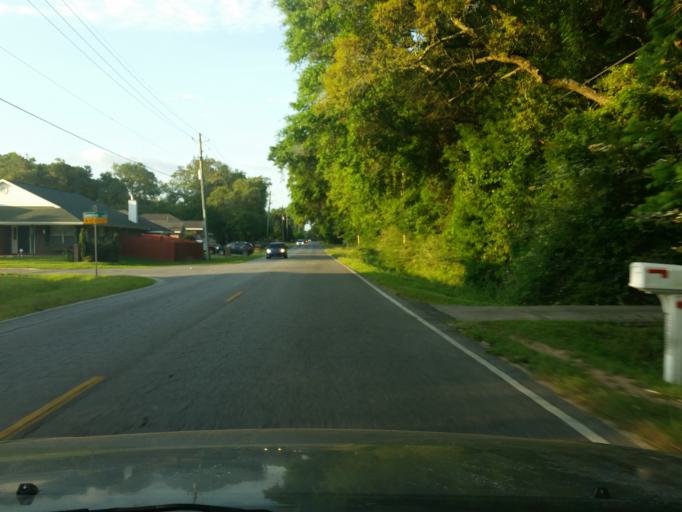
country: US
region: Florida
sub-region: Escambia County
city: Bellview
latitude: 30.4575
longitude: -87.3160
